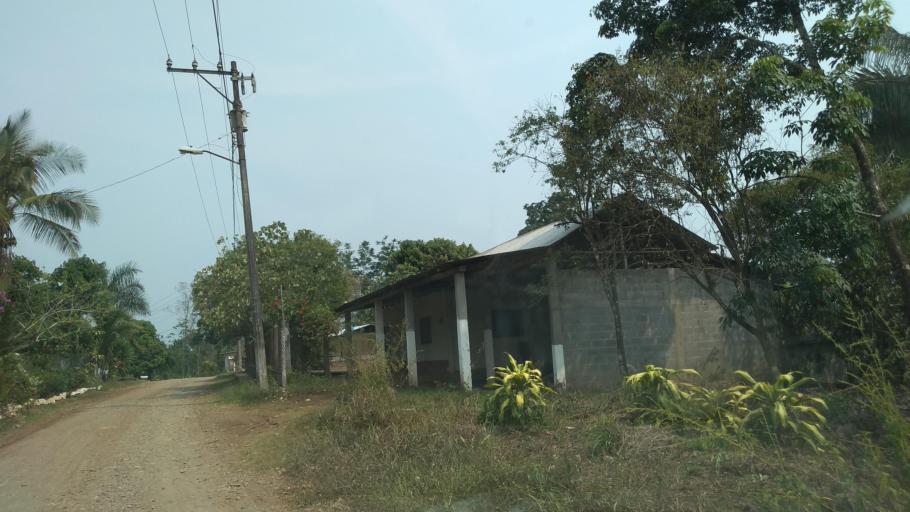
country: MX
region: Veracruz
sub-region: Tezonapa
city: Laguna Chica (Pueblo Nuevo)
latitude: 18.5498
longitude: -96.7815
